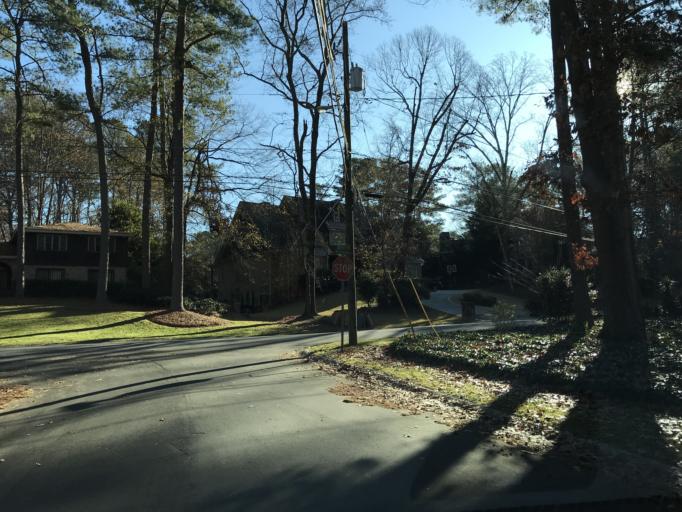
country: US
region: Georgia
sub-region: DeKalb County
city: North Atlanta
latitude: 33.8880
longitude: -84.3432
